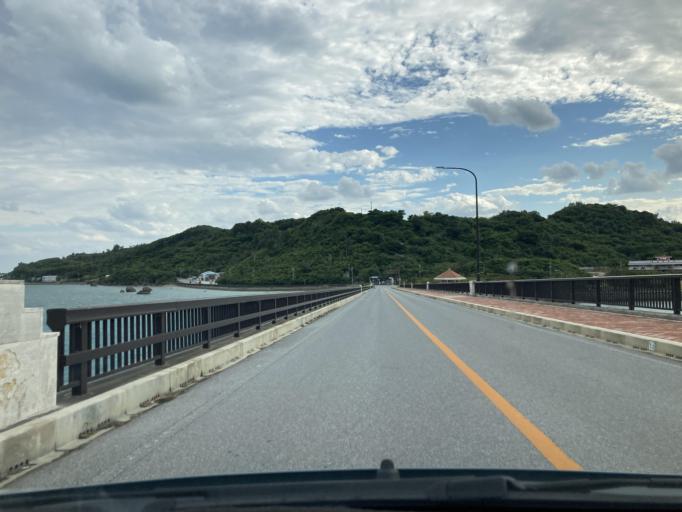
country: JP
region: Okinawa
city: Katsuren-haebaru
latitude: 26.3308
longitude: 127.9565
